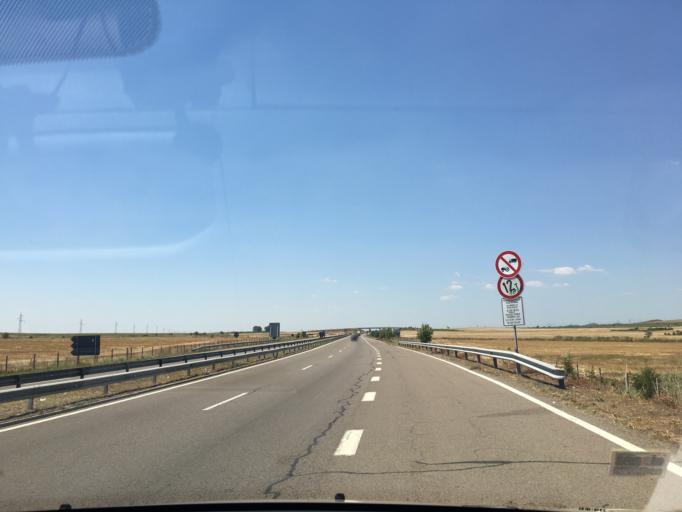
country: BG
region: Burgas
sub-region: Obshtina Kameno
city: Kameno
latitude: 42.5934
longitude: 27.3902
